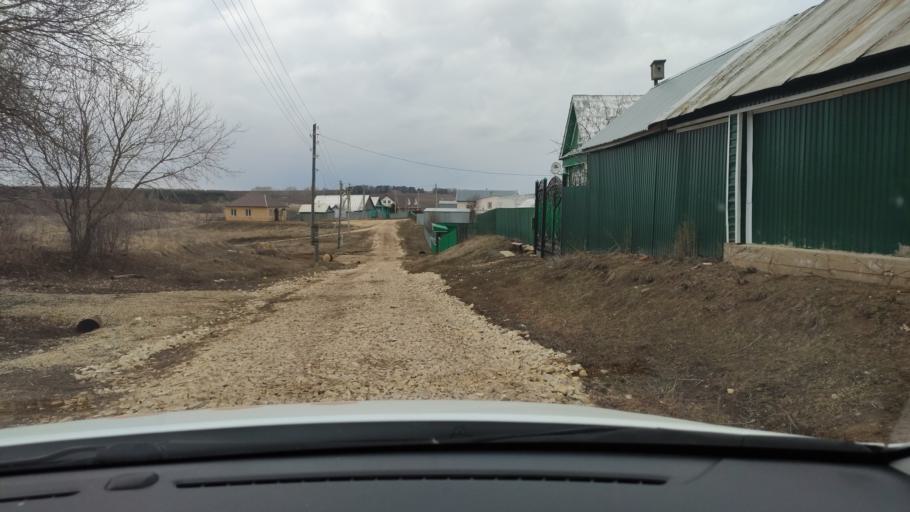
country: RU
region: Tatarstan
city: Vysokaya Gora
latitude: 56.2094
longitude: 49.3148
